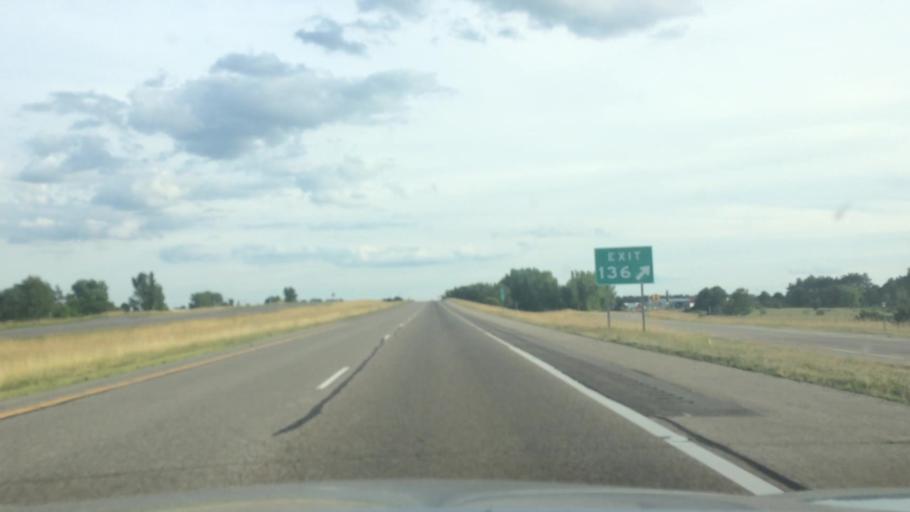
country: US
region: Wisconsin
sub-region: Portage County
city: Plover
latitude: 44.2178
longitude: -89.5248
